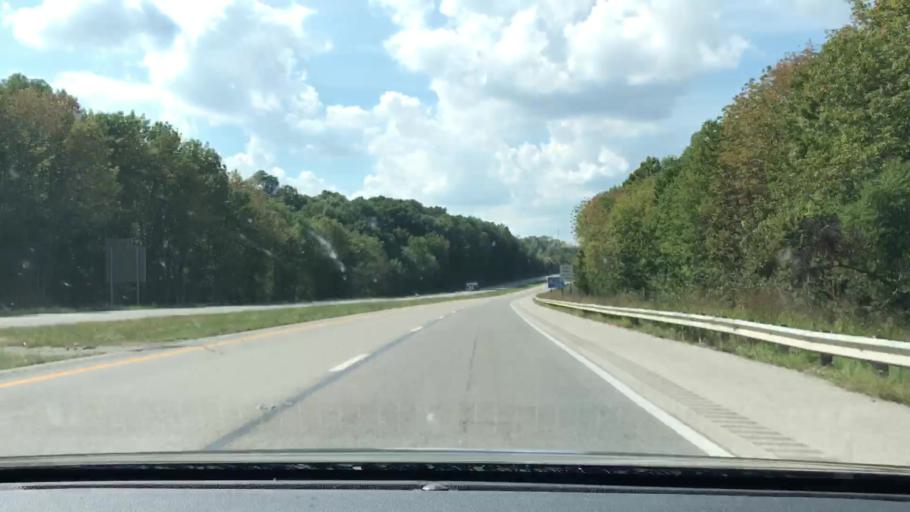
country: US
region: Kentucky
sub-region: Barren County
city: Glasgow
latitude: 36.9738
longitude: -85.9108
